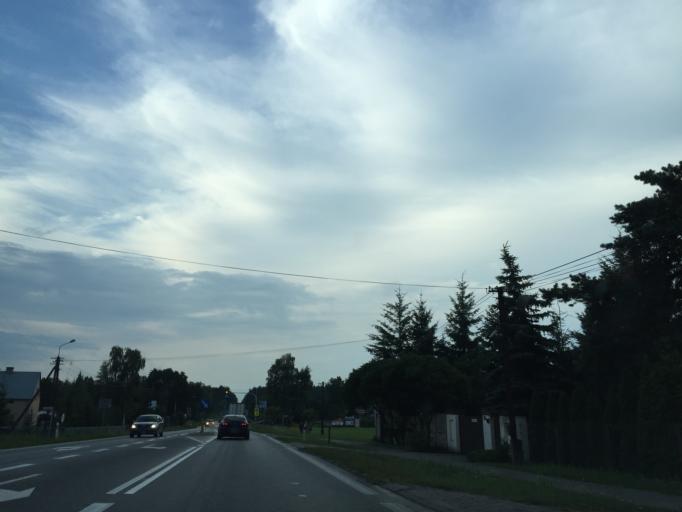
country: PL
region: Masovian Voivodeship
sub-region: Powiat ostrowski
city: Brok
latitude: 52.7009
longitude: 21.8465
